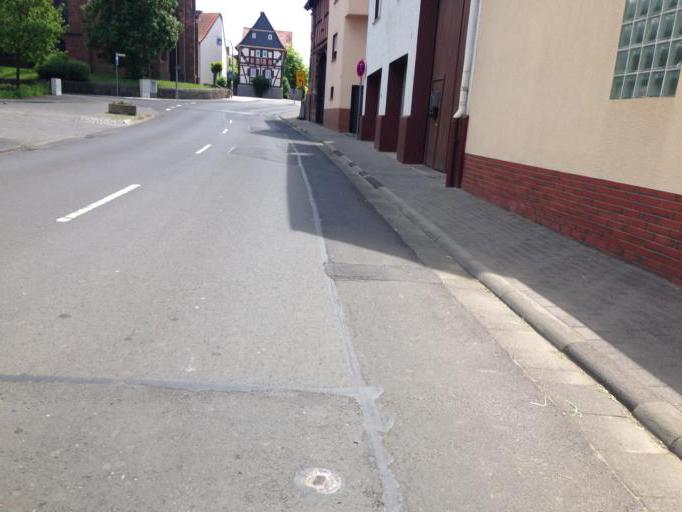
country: DE
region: Hesse
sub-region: Regierungsbezirk Giessen
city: Heuchelheim
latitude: 50.5908
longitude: 8.6114
